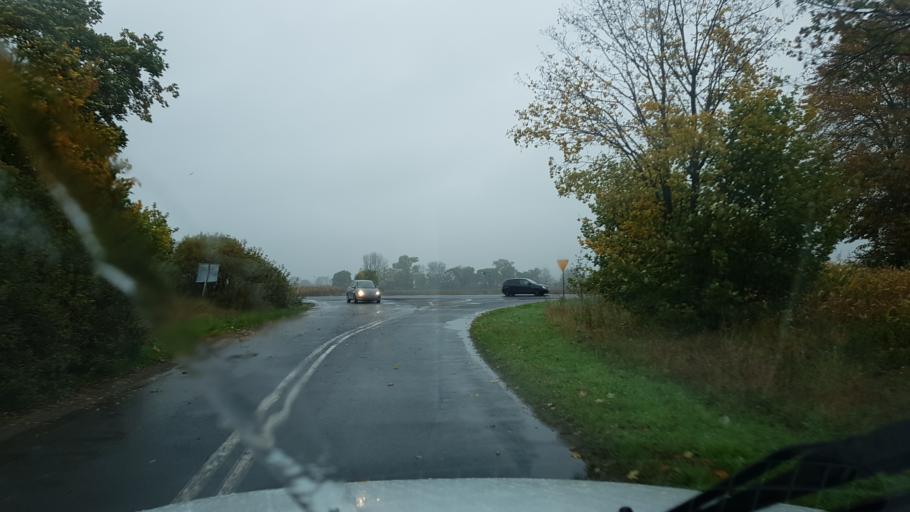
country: PL
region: West Pomeranian Voivodeship
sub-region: Powiat gryfinski
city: Stare Czarnowo
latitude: 53.2104
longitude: 14.8059
